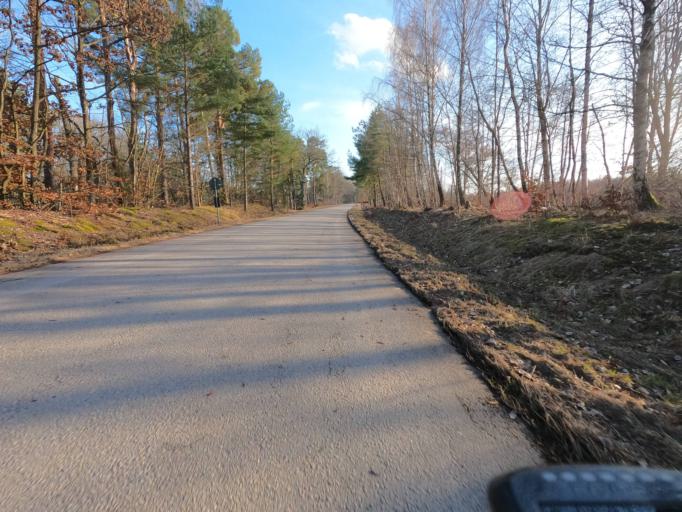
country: SE
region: Blekinge
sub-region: Karlshamns Kommun
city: Svangsta
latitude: 56.5259
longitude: 14.6744
